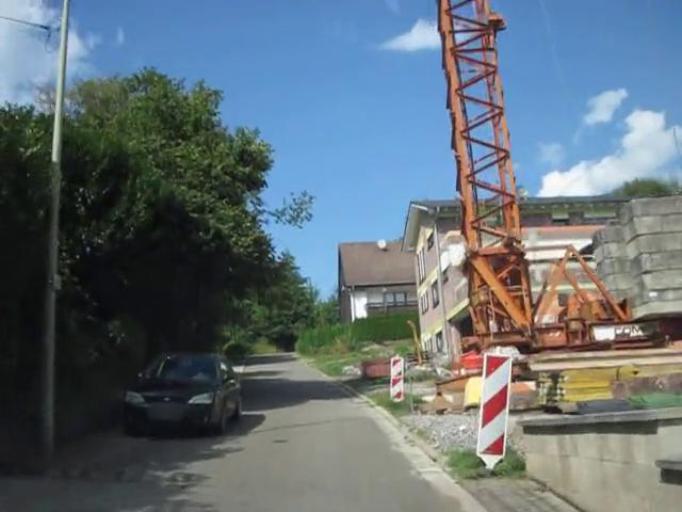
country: DE
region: Rheinland-Pfalz
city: Volkersweiler
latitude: 49.1653
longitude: 7.9225
